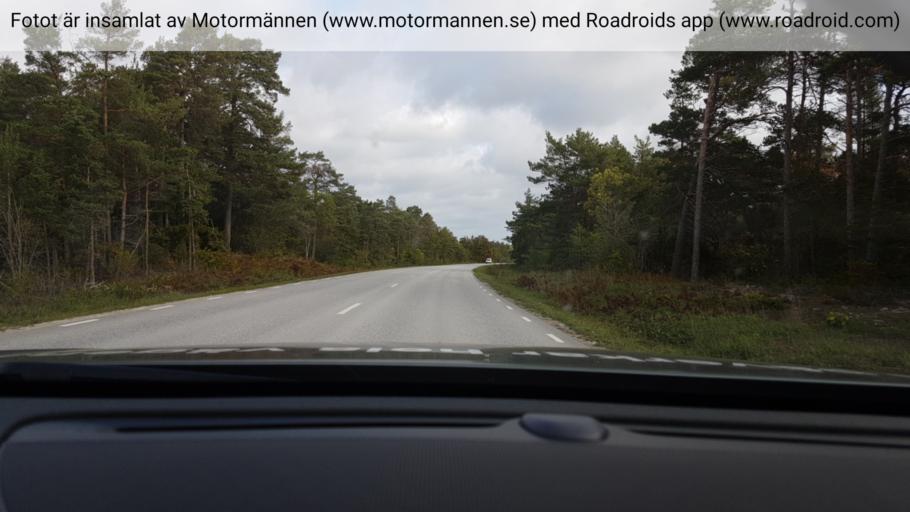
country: SE
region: Gotland
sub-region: Gotland
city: Slite
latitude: 57.7633
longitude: 18.7663
